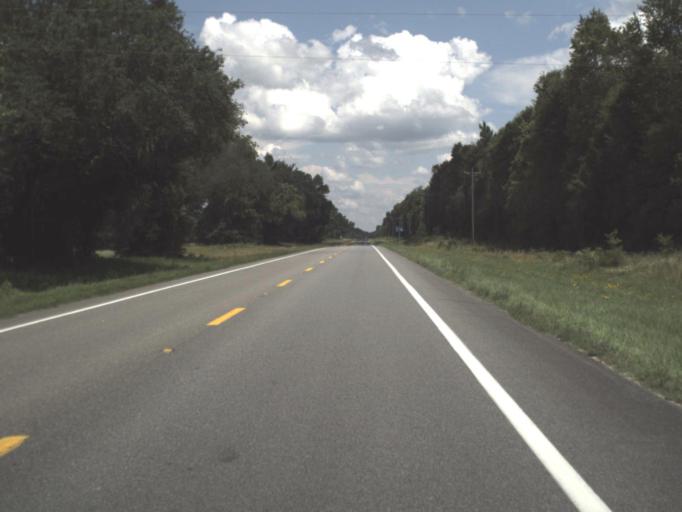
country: US
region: Florida
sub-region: Alachua County
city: High Springs
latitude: 29.9058
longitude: -82.6938
